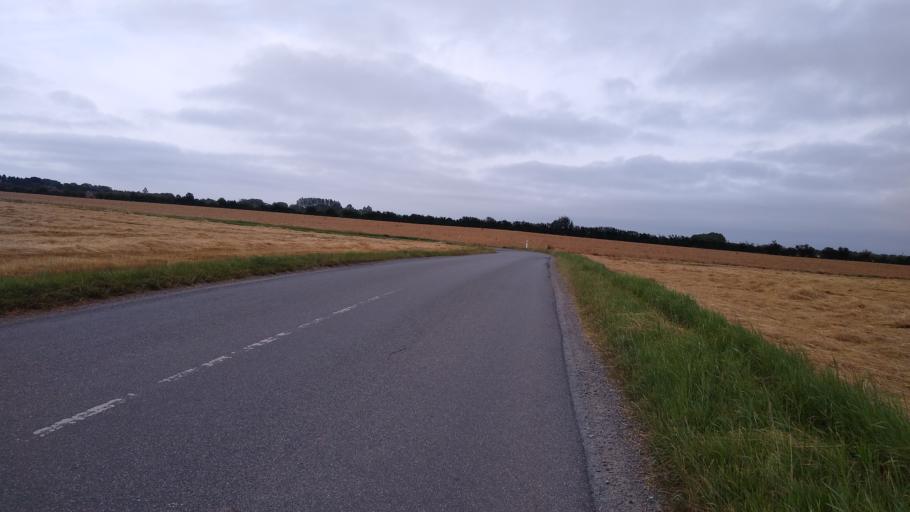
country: DK
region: South Denmark
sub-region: Vejle Kommune
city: Brejning
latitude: 55.6461
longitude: 9.6872
